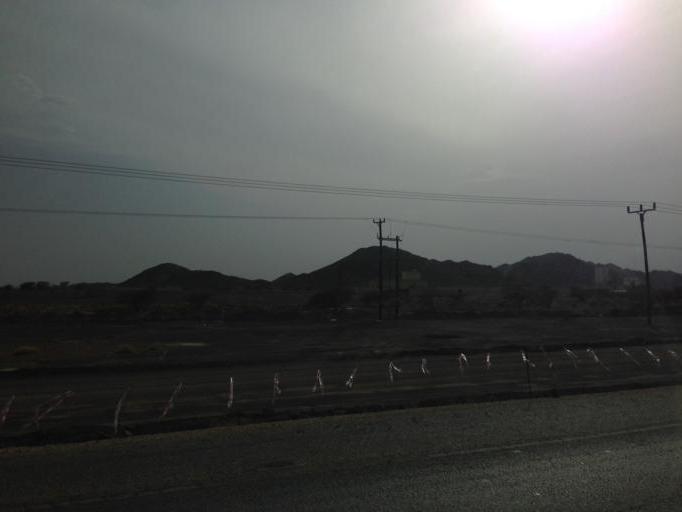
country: OM
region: Ash Sharqiyah
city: Al Qabil
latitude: 22.6365
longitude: 58.6420
